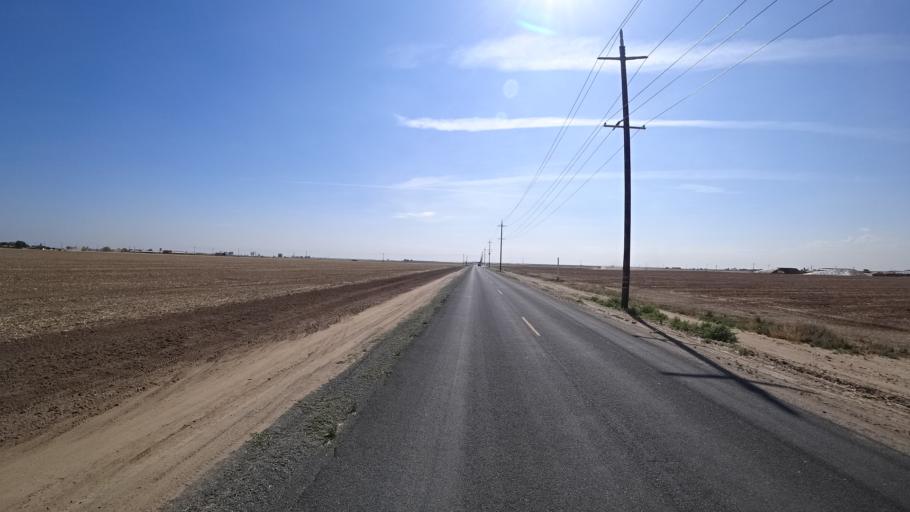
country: US
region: California
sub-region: Kings County
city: Home Garden
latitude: 36.2549
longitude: -119.6419
